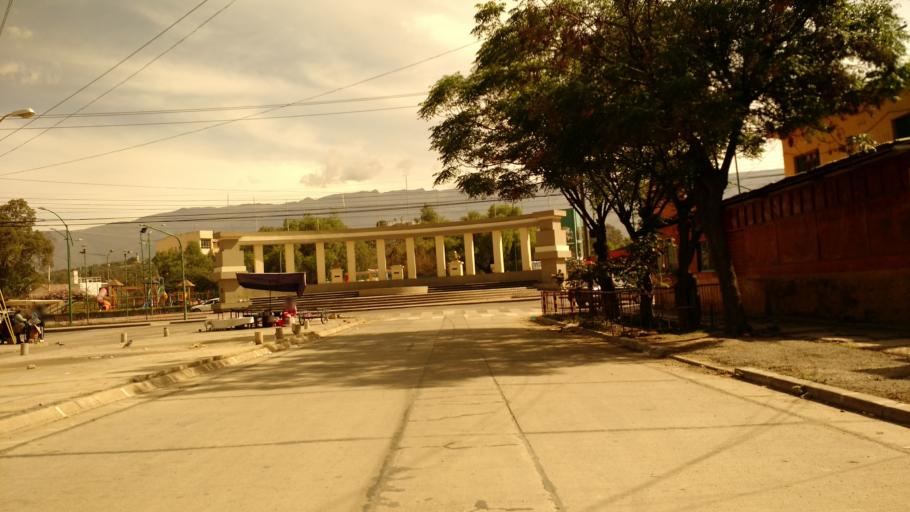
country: BO
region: Cochabamba
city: Cochabamba
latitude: -17.4137
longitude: -66.1587
